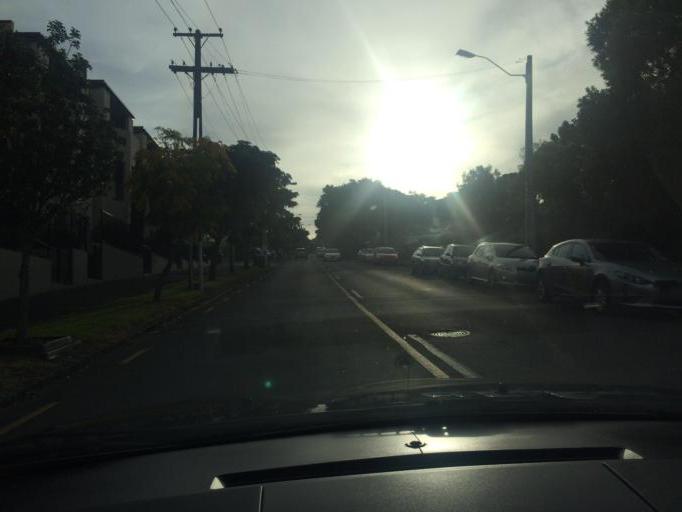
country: NZ
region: Auckland
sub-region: Auckland
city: Auckland
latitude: -36.8637
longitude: 174.7855
